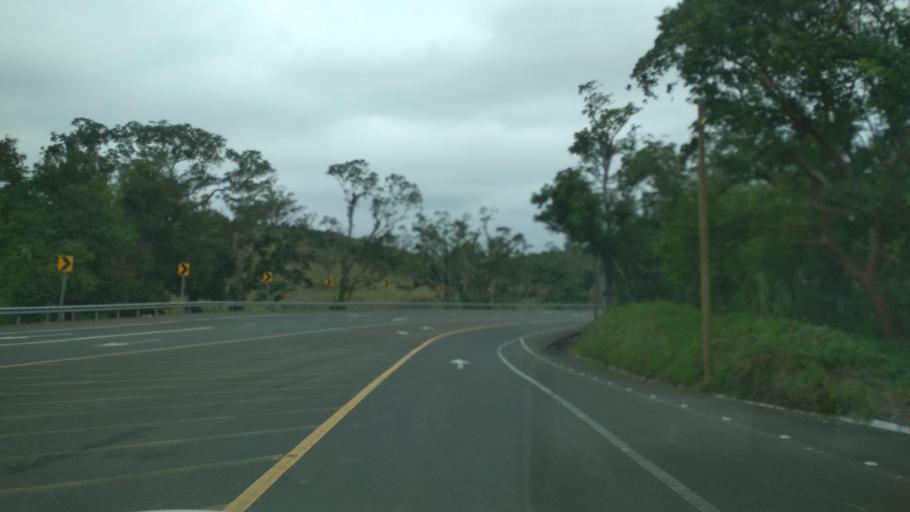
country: MX
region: Veracruz
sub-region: Papantla
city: Polutla
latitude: 20.4596
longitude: -97.2492
